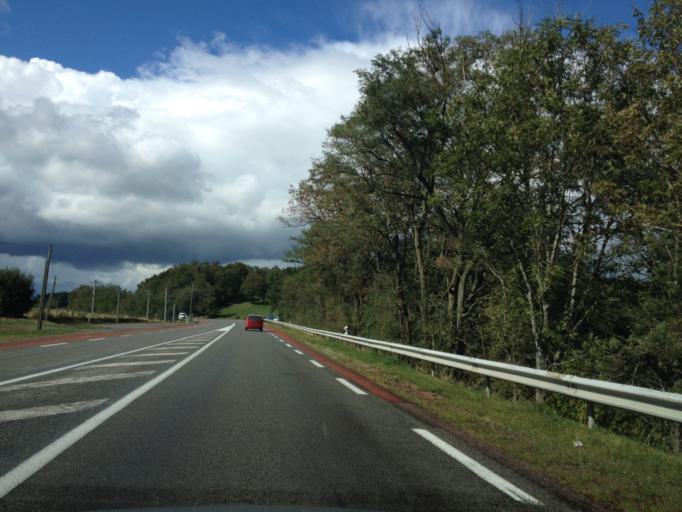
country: FR
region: Rhone-Alpes
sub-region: Departement du Rhone
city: Amplepuis
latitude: 45.9373
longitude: 4.2986
